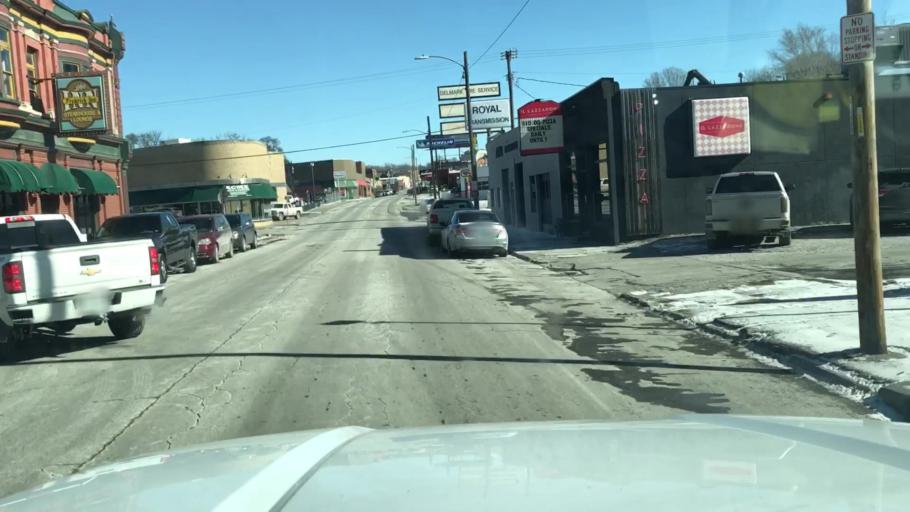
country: US
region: Missouri
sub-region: Buchanan County
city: Saint Joseph
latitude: 39.7722
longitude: -94.8408
